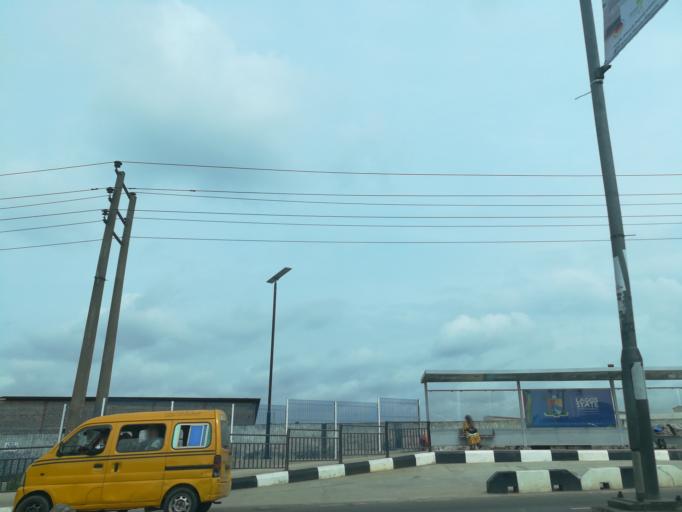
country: NG
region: Lagos
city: Ikeja
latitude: 6.6123
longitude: 3.3543
